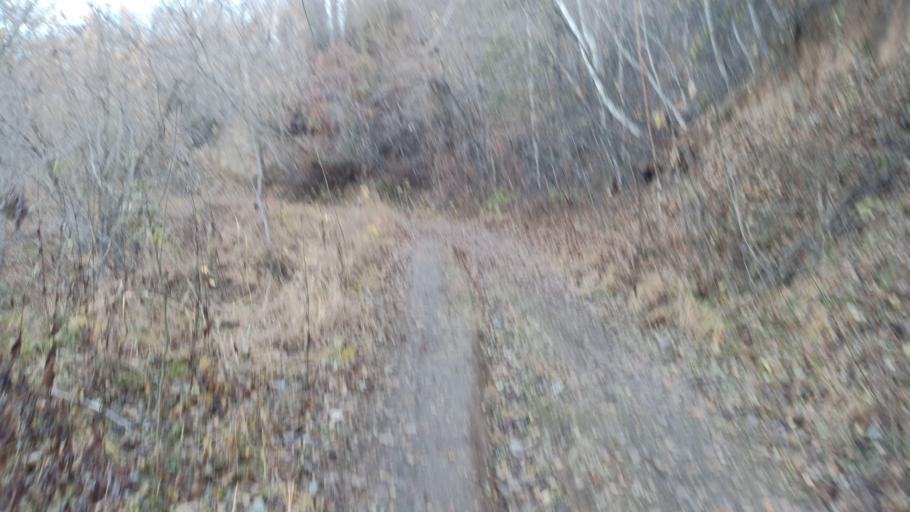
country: RU
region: Altai Krai
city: Gon'ba
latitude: 53.4340
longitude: 83.5530
